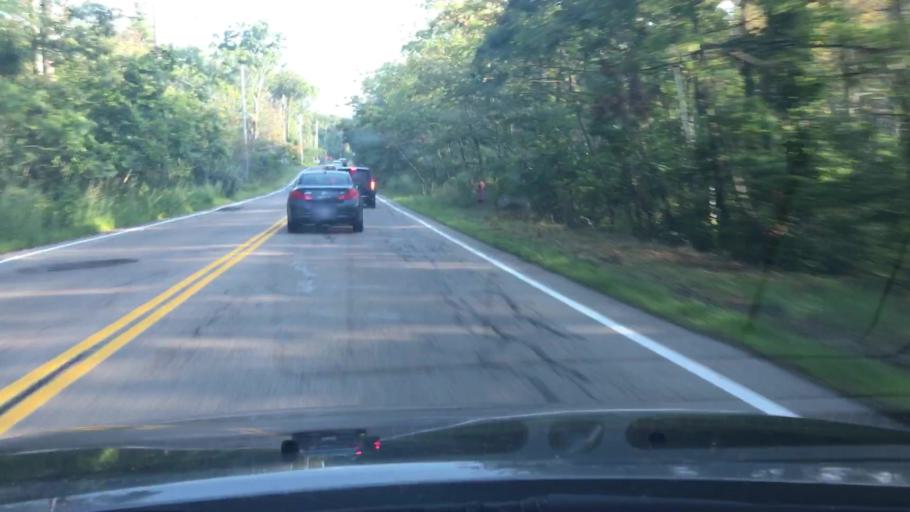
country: US
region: Massachusetts
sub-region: Middlesex County
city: Hopkinton
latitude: 42.1918
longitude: -71.5399
